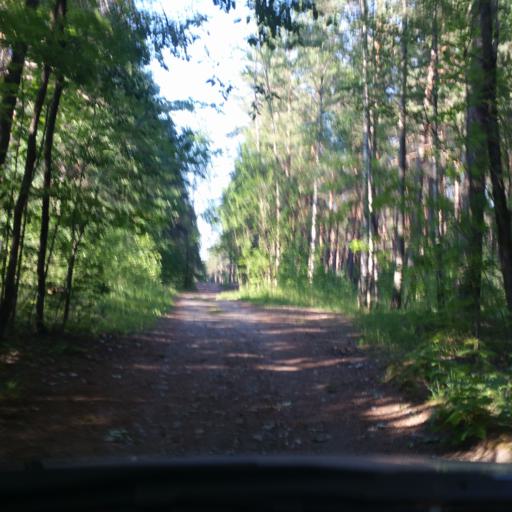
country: LV
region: Riga
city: Jaunciems
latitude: 56.9768
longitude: 24.2017
